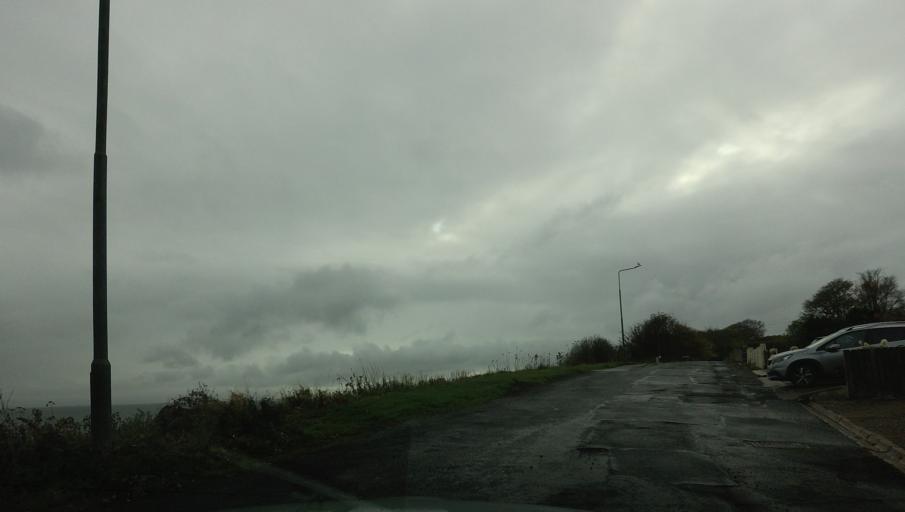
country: GB
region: Scotland
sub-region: Fife
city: East Wemyss
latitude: 56.1546
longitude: -3.0704
